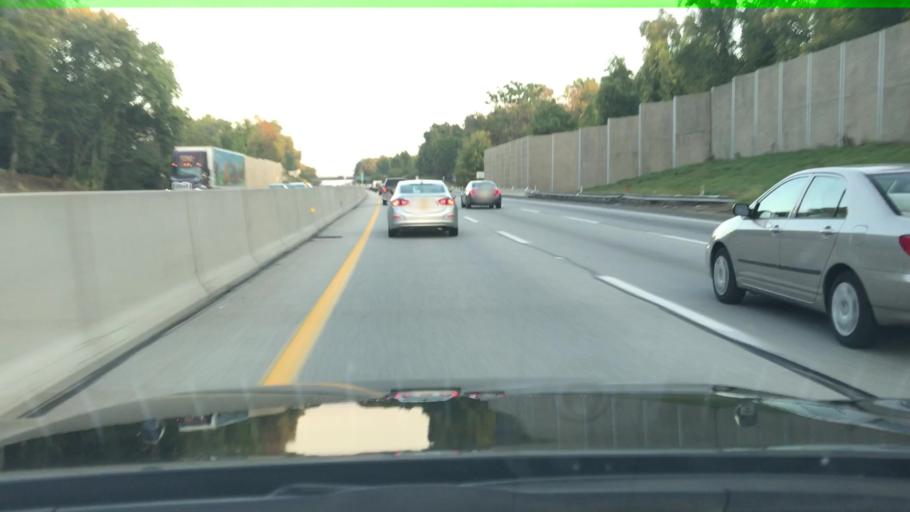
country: US
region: Pennsylvania
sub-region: Bucks County
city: Feasterville
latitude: 40.1537
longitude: -75.0304
